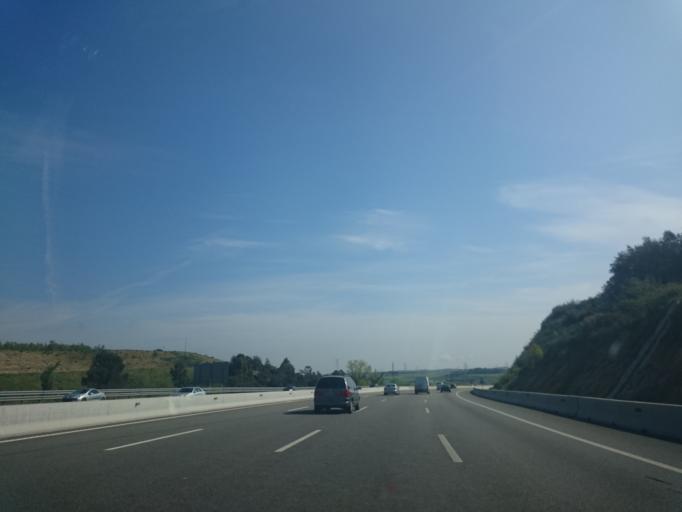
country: ES
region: Catalonia
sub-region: Provincia de Girona
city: Sant Julia de Ramis
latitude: 42.0416
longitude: 2.8419
